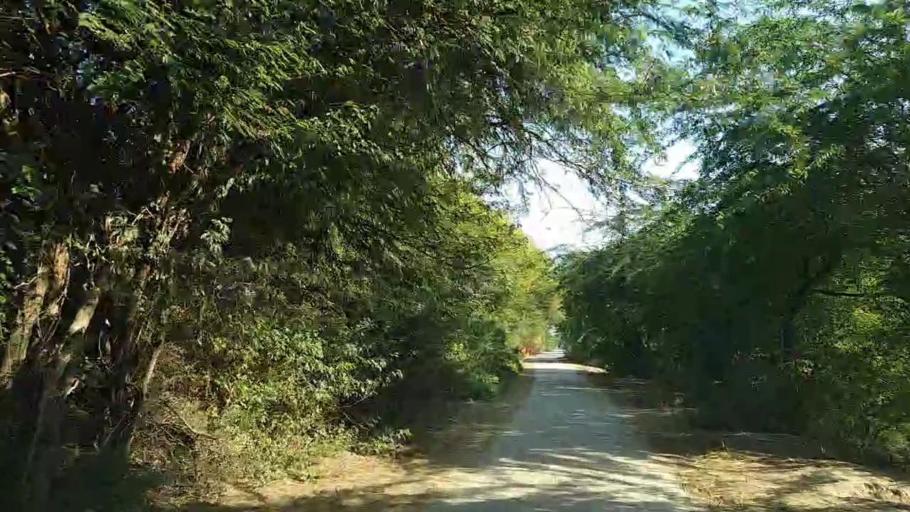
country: PK
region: Sindh
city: Bulri
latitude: 24.7923
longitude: 68.3437
